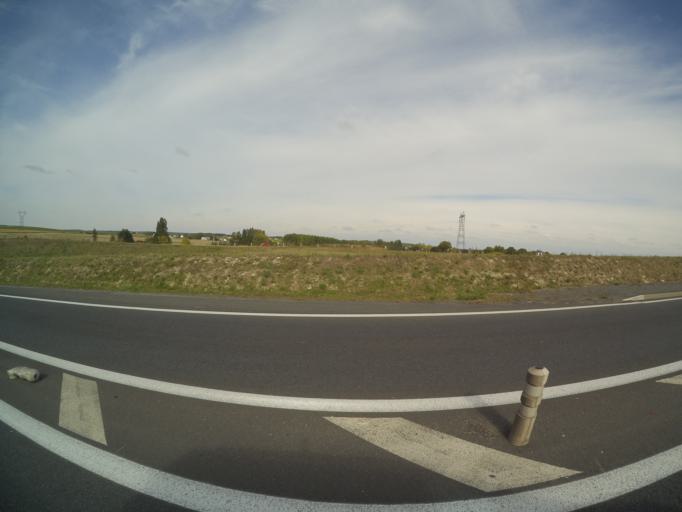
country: FR
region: Pays de la Loire
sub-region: Departement de Maine-et-Loire
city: Distre
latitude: 47.2140
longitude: -0.1771
